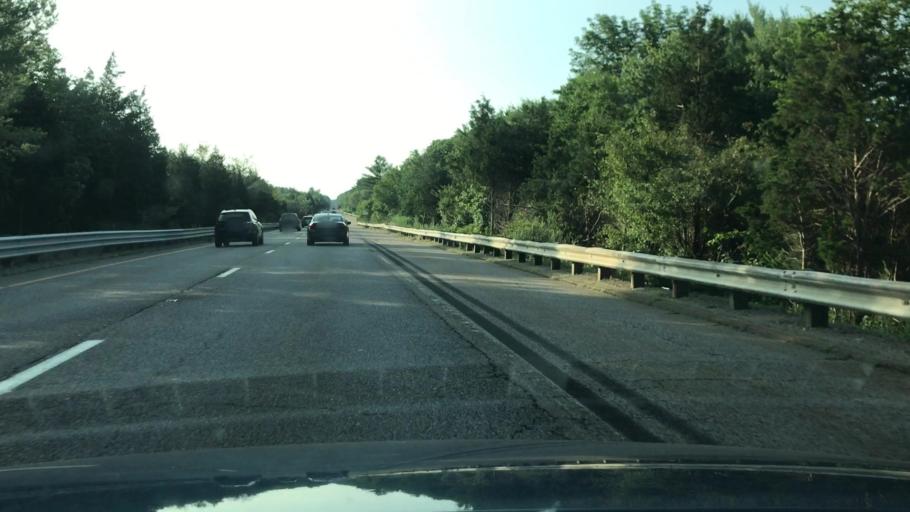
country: US
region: Massachusetts
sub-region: Plymouth County
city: Hanover
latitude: 42.1429
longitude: -70.8299
